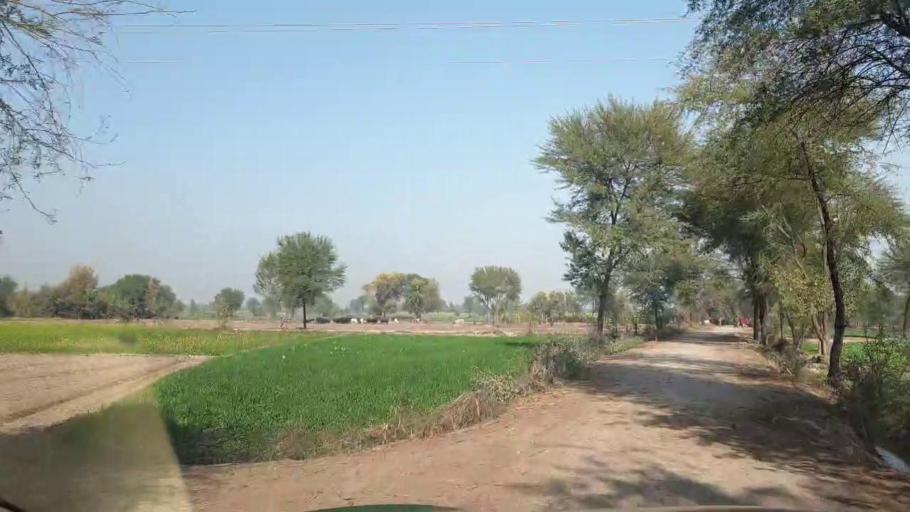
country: PK
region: Sindh
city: Ubauro
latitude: 28.1115
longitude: 69.7739
